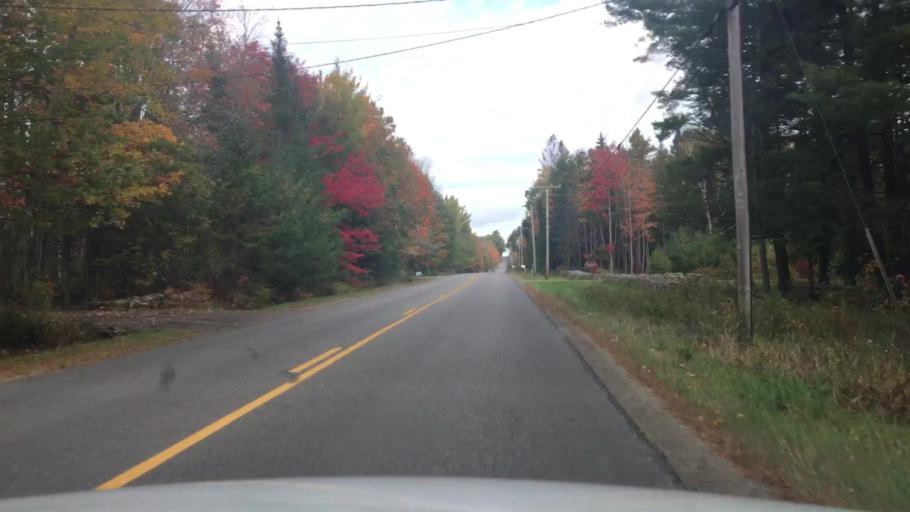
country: US
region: Maine
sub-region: Waldo County
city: Searsmont
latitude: 44.3832
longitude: -69.1320
